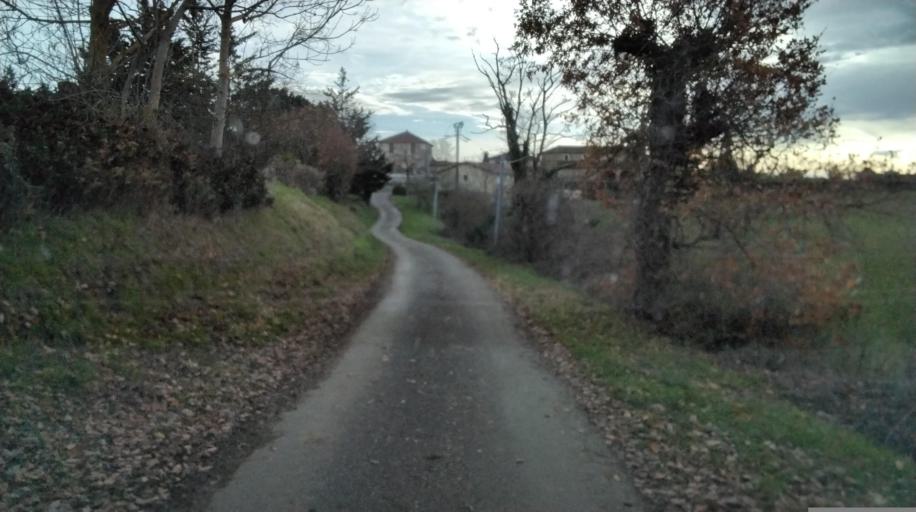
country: FR
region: Midi-Pyrenees
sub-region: Departement de la Haute-Garonne
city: Le Fousseret
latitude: 43.2997
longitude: 0.9827
